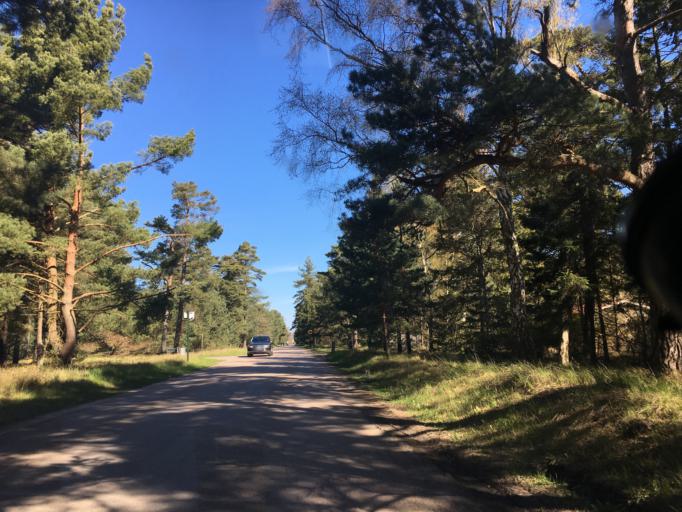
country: SE
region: Skane
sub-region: Vellinge Kommun
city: Ljunghusen
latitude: 55.3998
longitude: 12.9220
